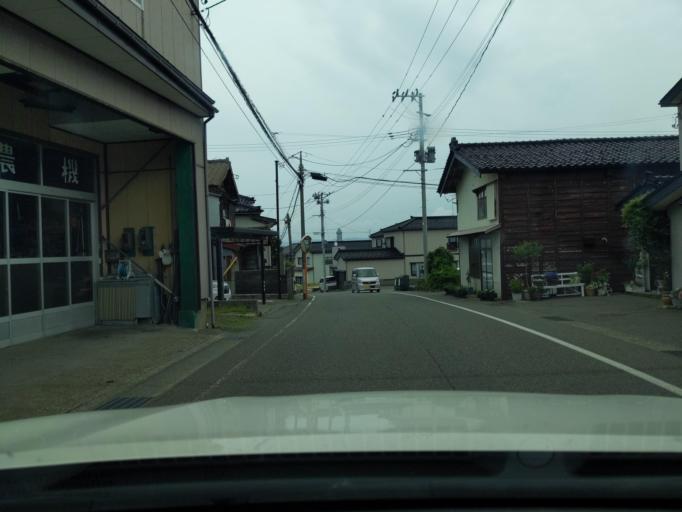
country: JP
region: Niigata
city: Kashiwazaki
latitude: 37.3632
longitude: 138.5451
